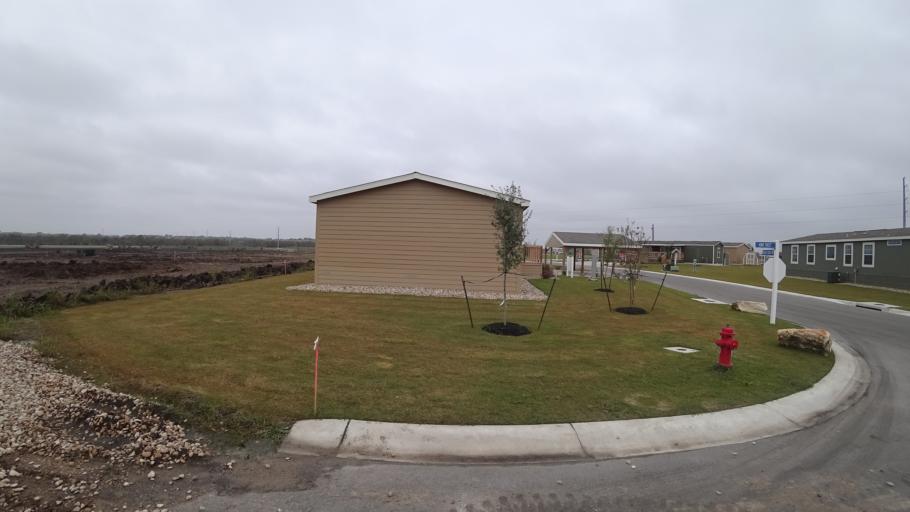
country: US
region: Texas
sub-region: Travis County
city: Pflugerville
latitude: 30.4073
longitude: -97.6065
